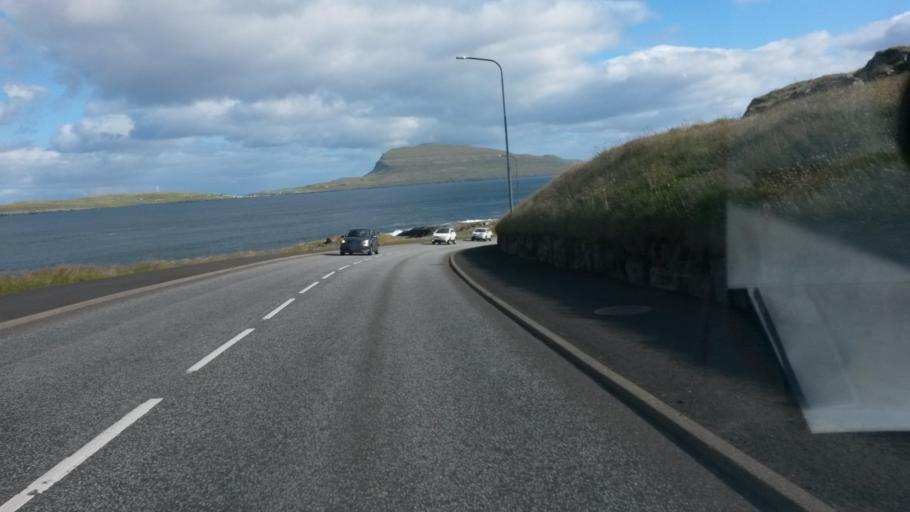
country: FO
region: Streymoy
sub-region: Torshavn
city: Torshavn
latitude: 62.0233
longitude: -6.7608
